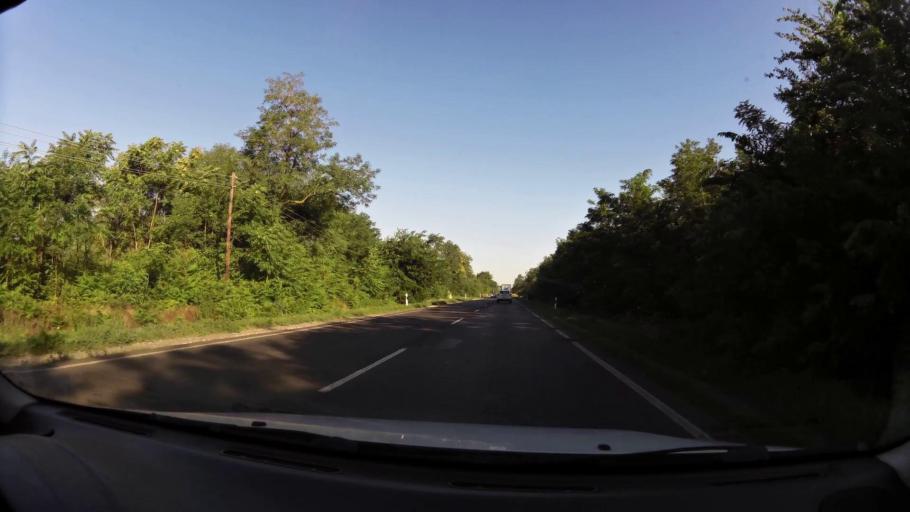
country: HU
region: Pest
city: Pilis
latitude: 47.2720
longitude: 19.5661
